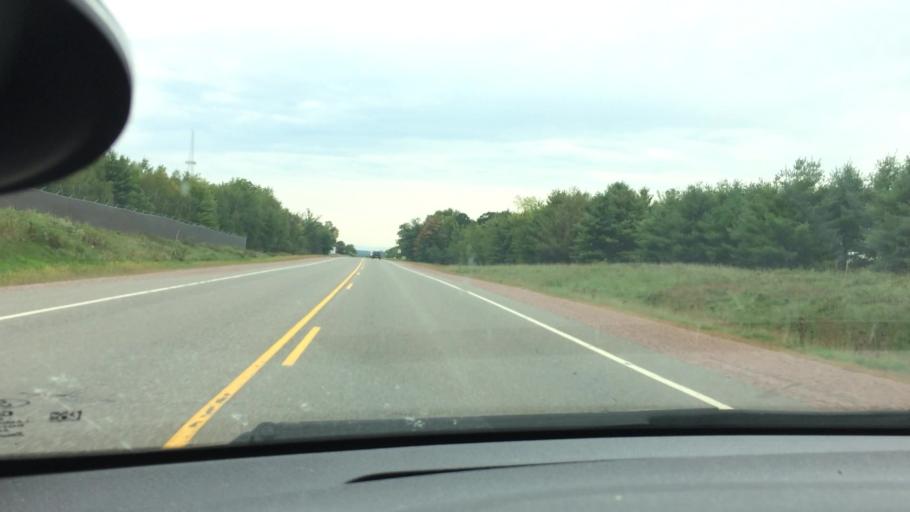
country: US
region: Wisconsin
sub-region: Clark County
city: Neillsville
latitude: 44.5623
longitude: -90.6510
